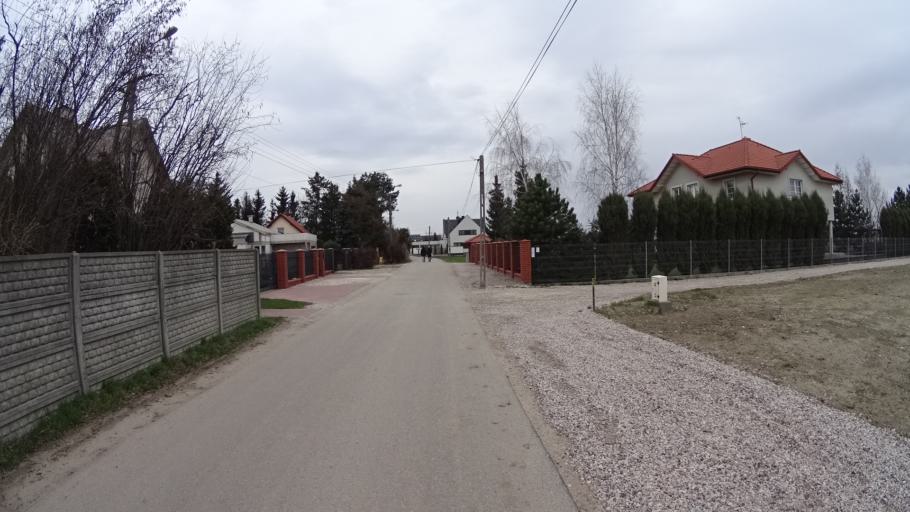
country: PL
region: Masovian Voivodeship
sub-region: Powiat warszawski zachodni
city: Stare Babice
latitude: 52.2443
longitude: 20.8253
